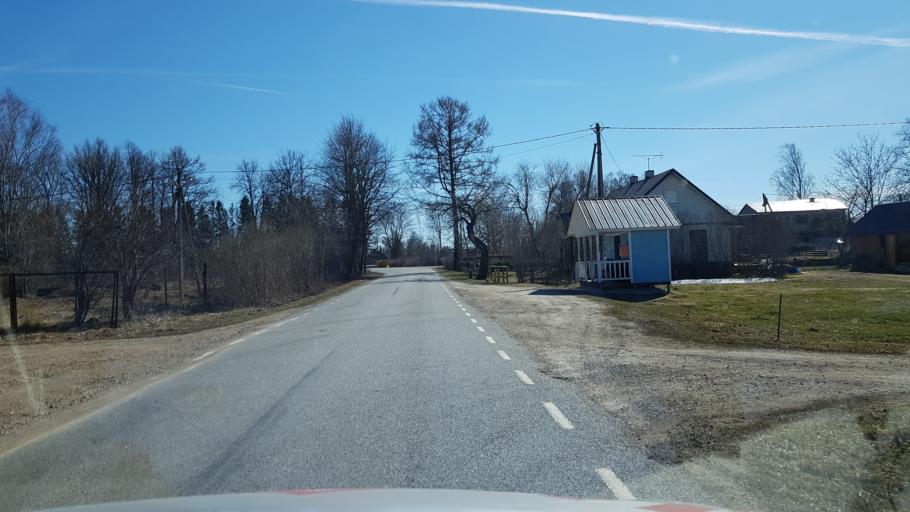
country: EE
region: Laeaene-Virumaa
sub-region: Viru-Nigula vald
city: Kunda
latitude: 59.3464
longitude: 26.6757
